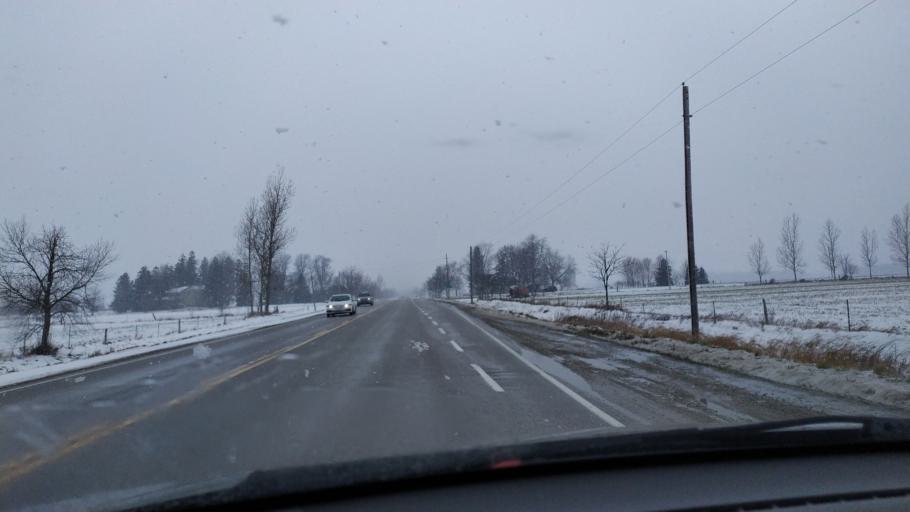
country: CA
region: Ontario
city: Stratford
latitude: 43.5059
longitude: -80.8878
